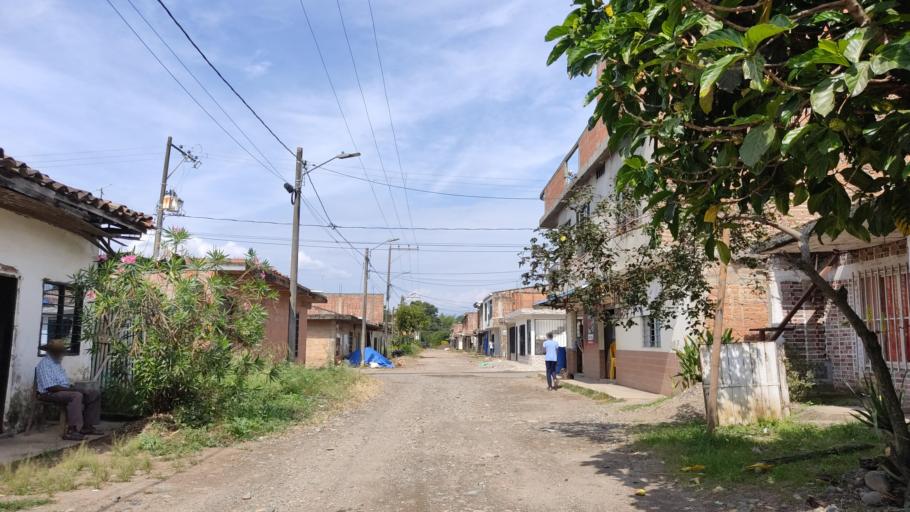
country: CO
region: Cauca
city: Buenos Aires
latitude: 3.1279
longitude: -76.5917
